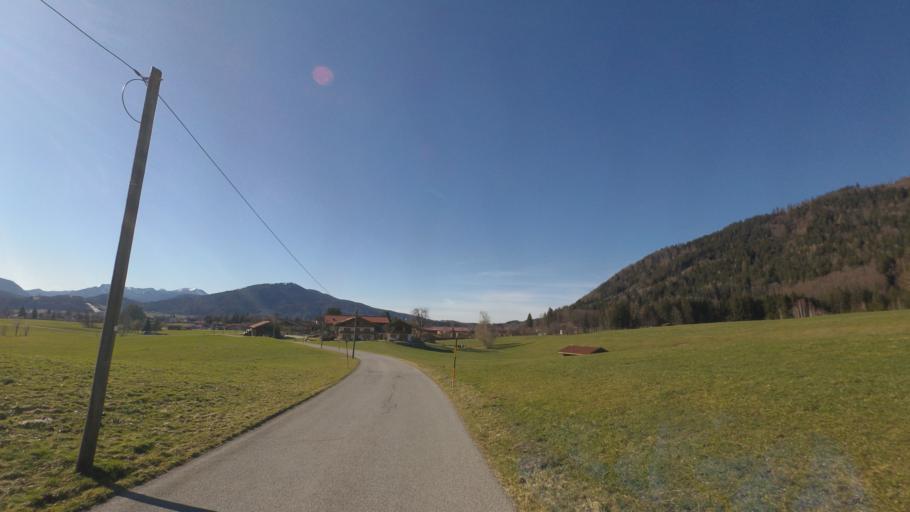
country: DE
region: Bavaria
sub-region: Upper Bavaria
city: Inzell
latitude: 47.7682
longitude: 12.7753
